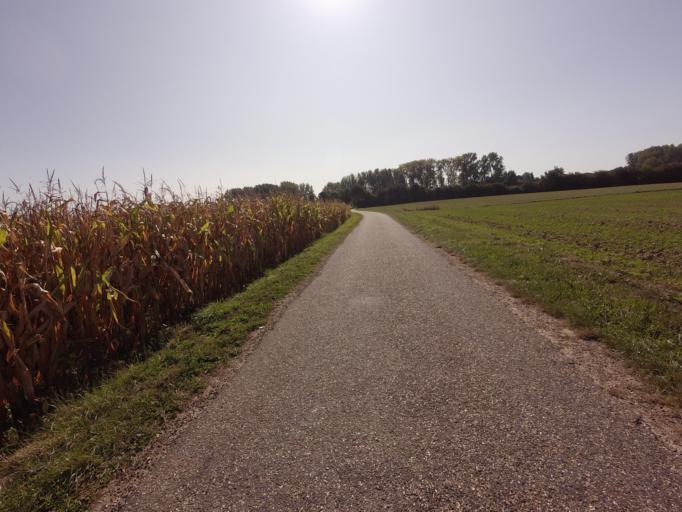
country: NL
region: Limburg
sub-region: Gemeente Roerdalen
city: Melick
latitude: 51.1500
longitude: 6.0336
